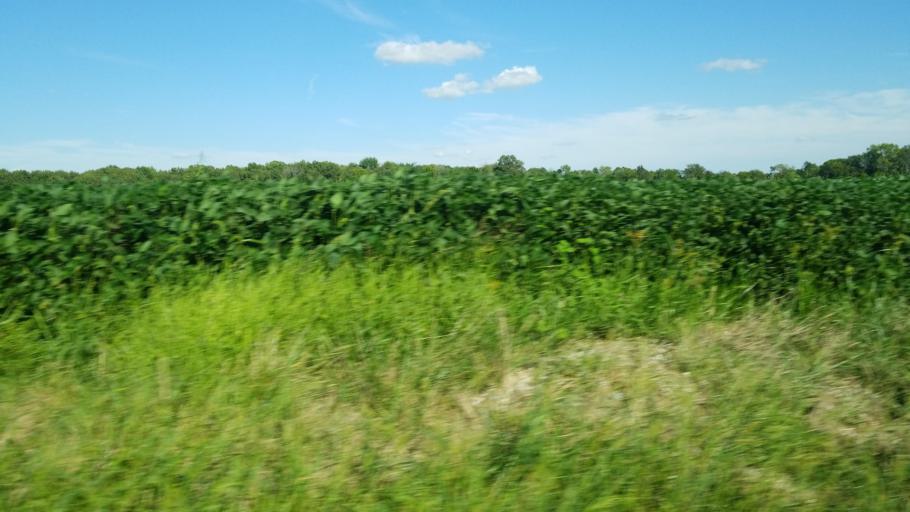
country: US
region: Illinois
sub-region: Saline County
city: Harrisburg
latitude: 37.8167
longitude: -88.5672
